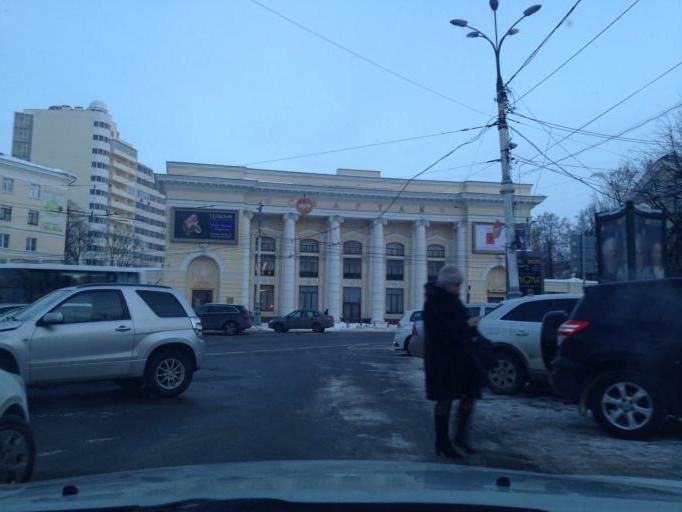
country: RU
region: Voronezj
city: Voronezh
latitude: 51.6628
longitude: 39.2034
